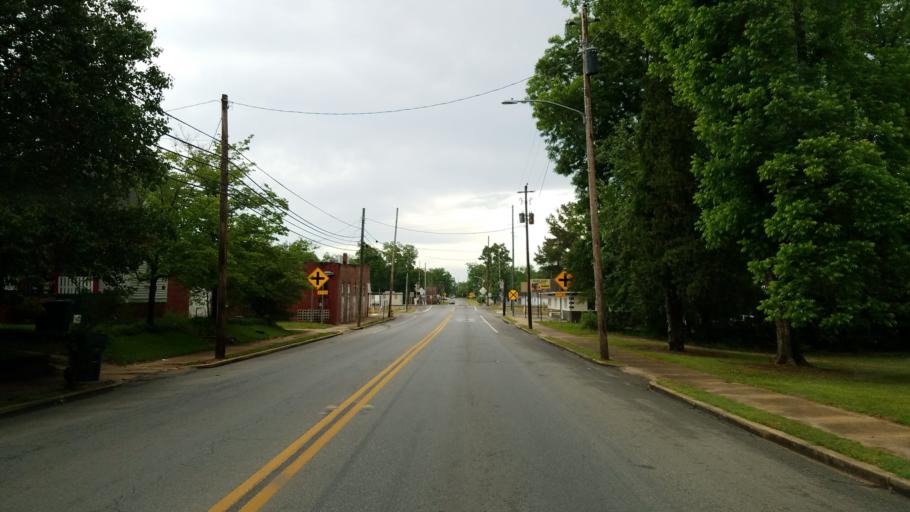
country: US
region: Georgia
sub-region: Dooly County
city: Vienna
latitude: 32.0906
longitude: -83.7886
